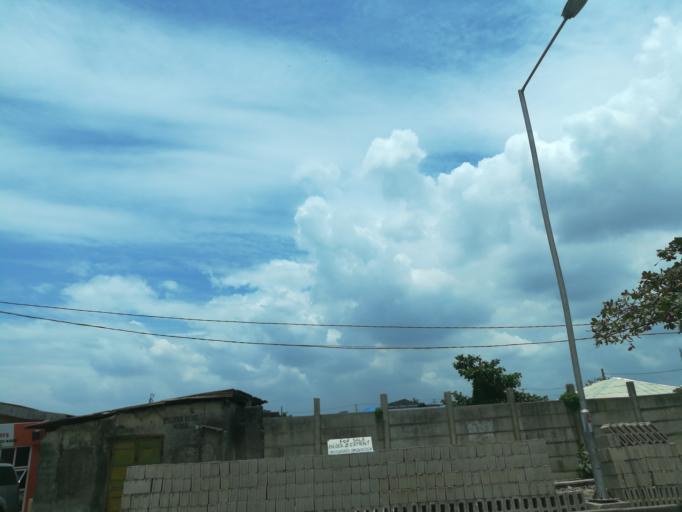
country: NG
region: Lagos
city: Ebute Ikorodu
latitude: 6.6027
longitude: 3.4870
